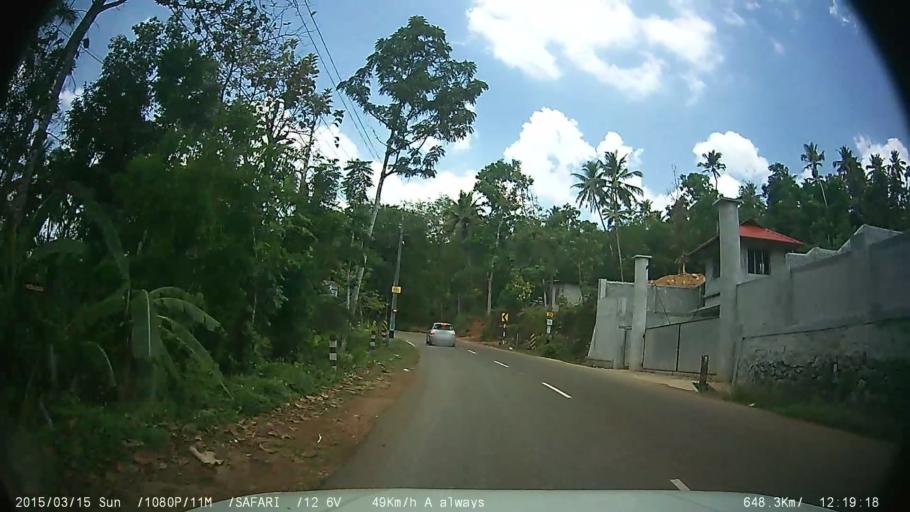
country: IN
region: Kerala
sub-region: Kottayam
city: Palackattumala
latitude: 9.7589
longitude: 76.5827
